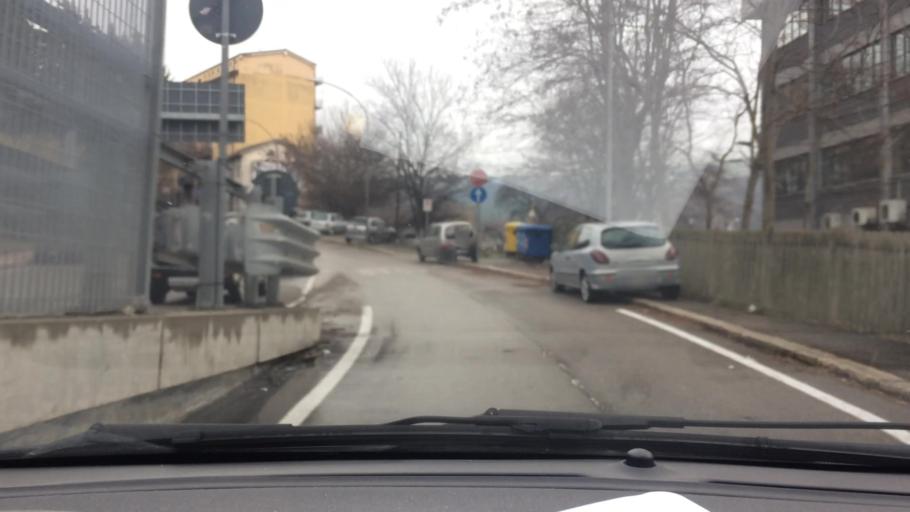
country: IT
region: Basilicate
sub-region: Provincia di Potenza
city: Potenza
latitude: 40.6282
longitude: 15.7982
